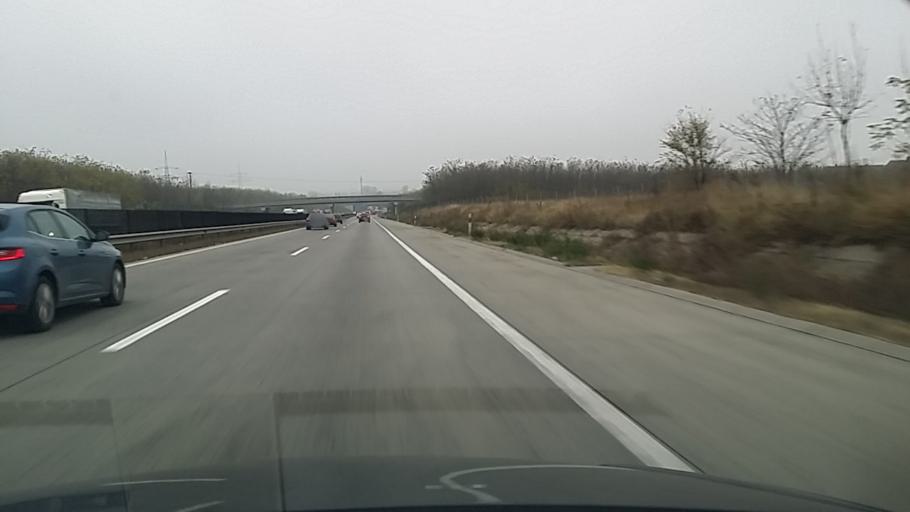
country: HU
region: Pest
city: Ecser
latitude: 47.4480
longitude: 19.3320
